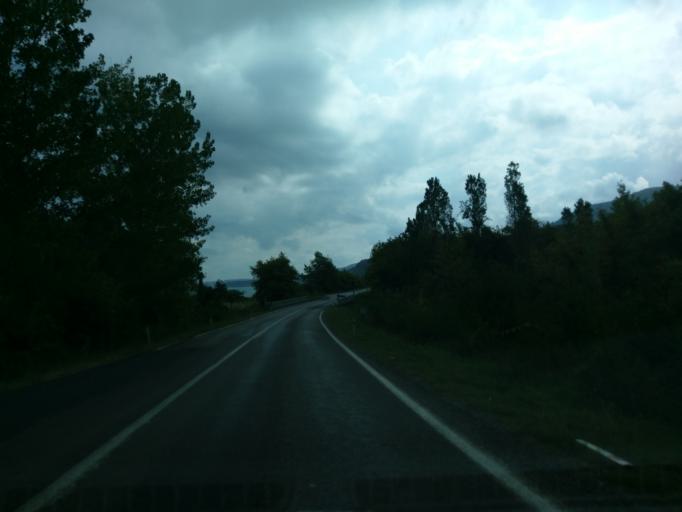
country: TR
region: Sinop
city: Ayancik
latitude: 41.9452
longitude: 34.6925
